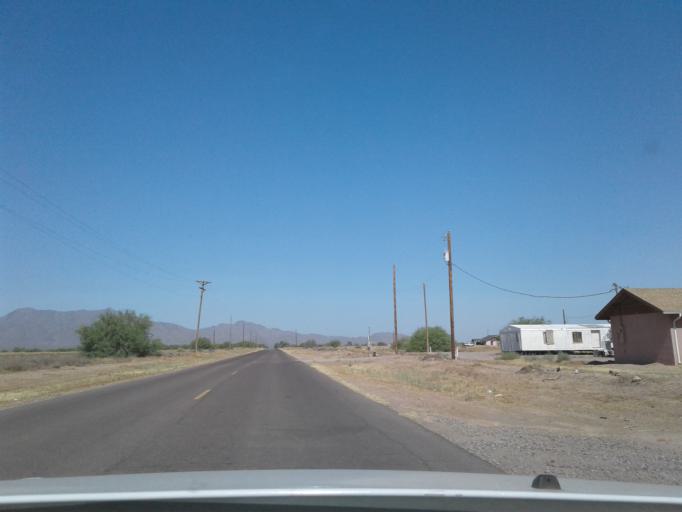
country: US
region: Arizona
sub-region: Maricopa County
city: Laveen
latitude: 33.3340
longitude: -112.1907
